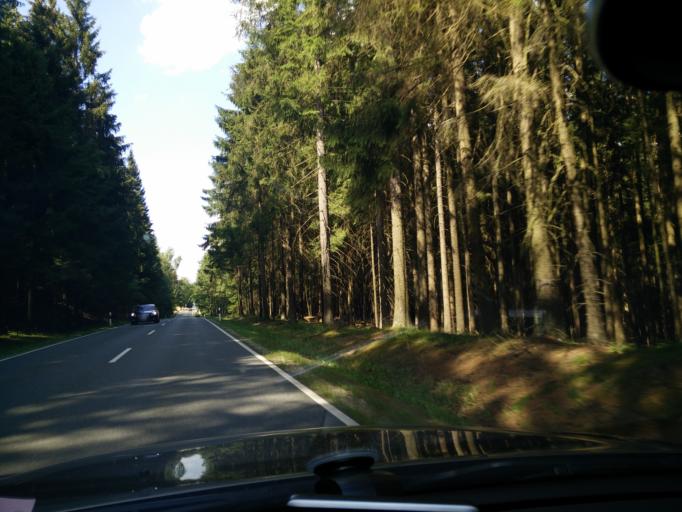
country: DE
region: Bavaria
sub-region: Upper Franconia
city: Roslau
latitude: 50.0634
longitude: 11.9739
